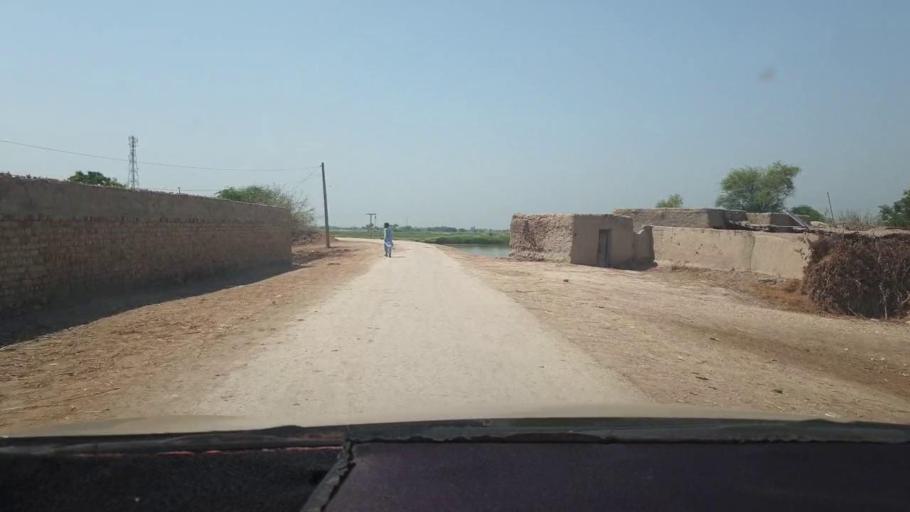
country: PK
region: Sindh
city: Miro Khan
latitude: 27.6613
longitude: 68.0822
